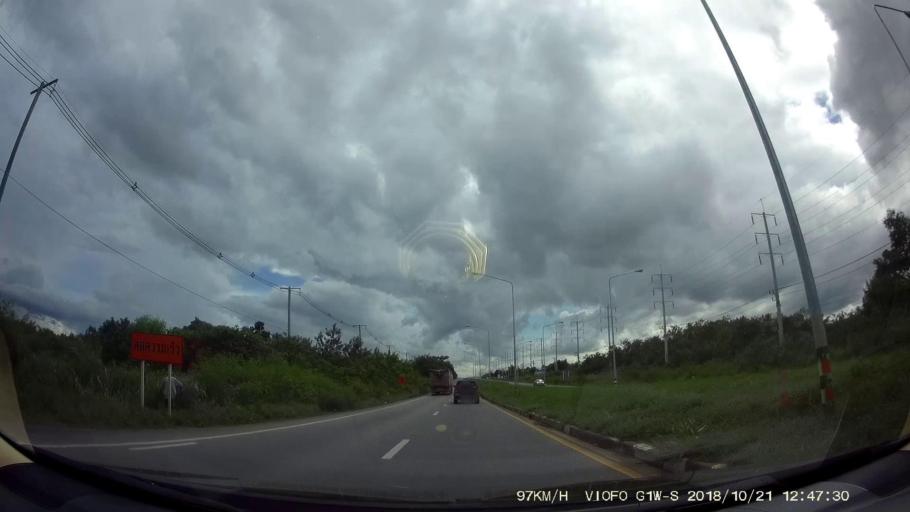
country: TH
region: Nakhon Ratchasima
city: Amphoe Sikhiu
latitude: 14.9274
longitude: 101.6839
